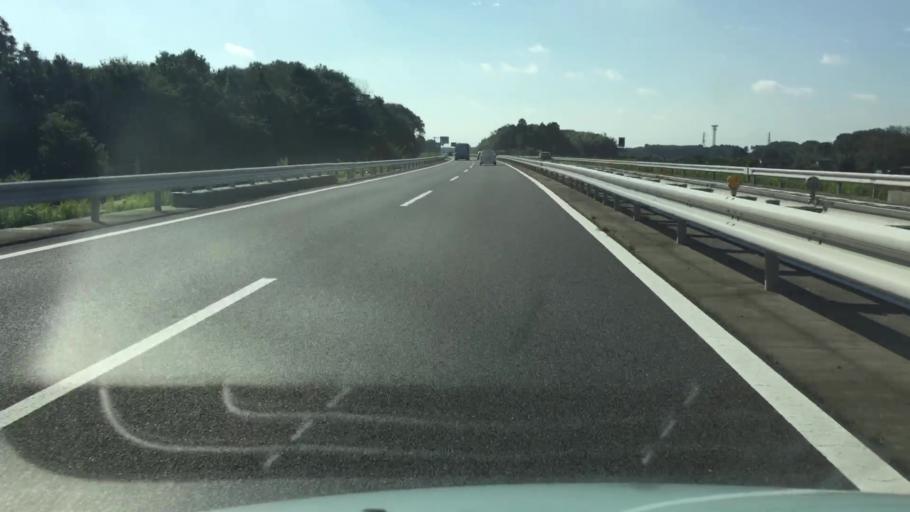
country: JP
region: Tochigi
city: Mooka
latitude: 36.4996
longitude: 139.9892
